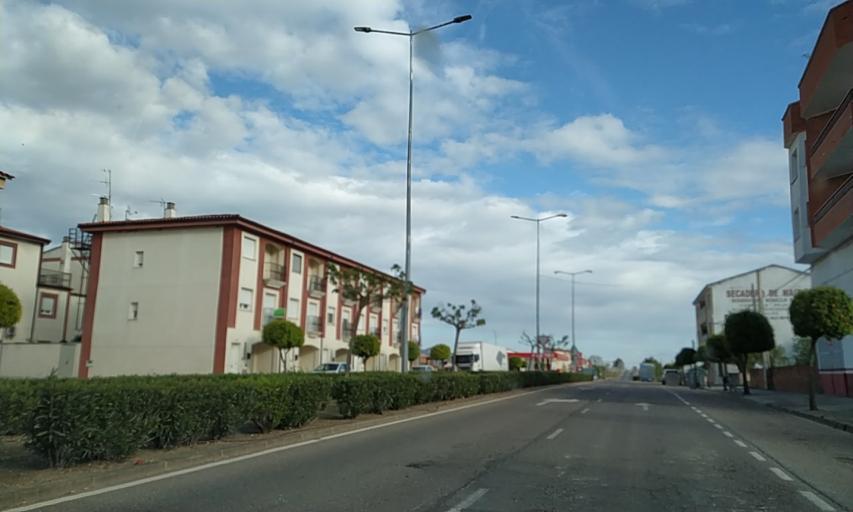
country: ES
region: Extremadura
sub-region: Provincia de Caceres
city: Moraleja
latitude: 40.0645
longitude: -6.6525
